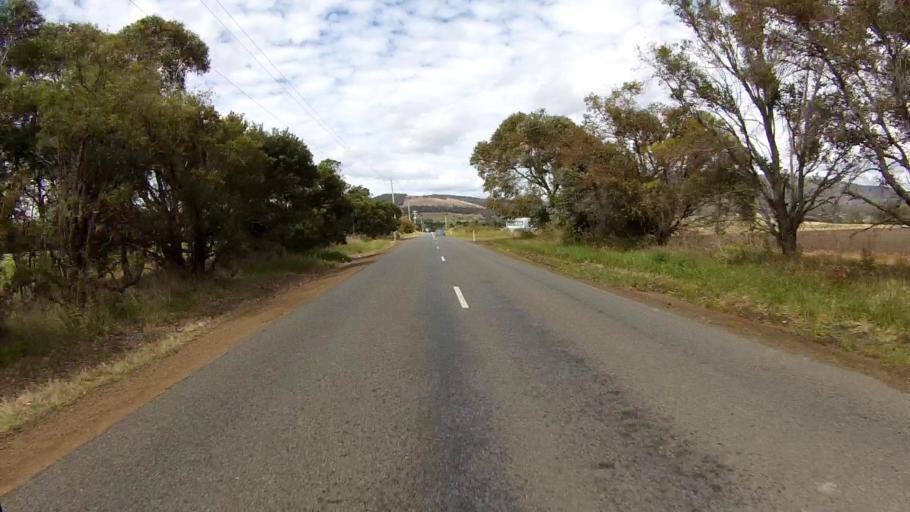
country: AU
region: Tasmania
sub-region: Clarence
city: Cambridge
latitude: -42.7536
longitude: 147.4081
